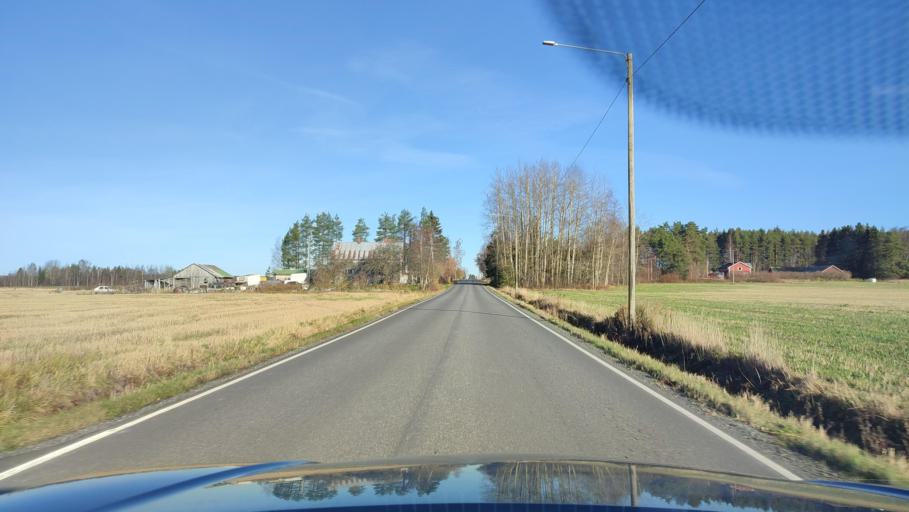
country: FI
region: Southern Ostrobothnia
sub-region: Suupohja
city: Karijoki
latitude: 62.2865
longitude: 21.7165
